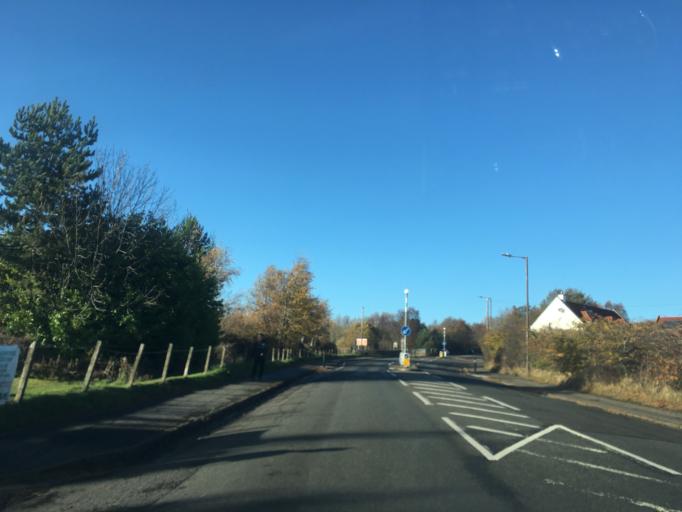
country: GB
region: Scotland
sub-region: Midlothian
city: Loanhead
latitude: 55.9134
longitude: -3.1767
